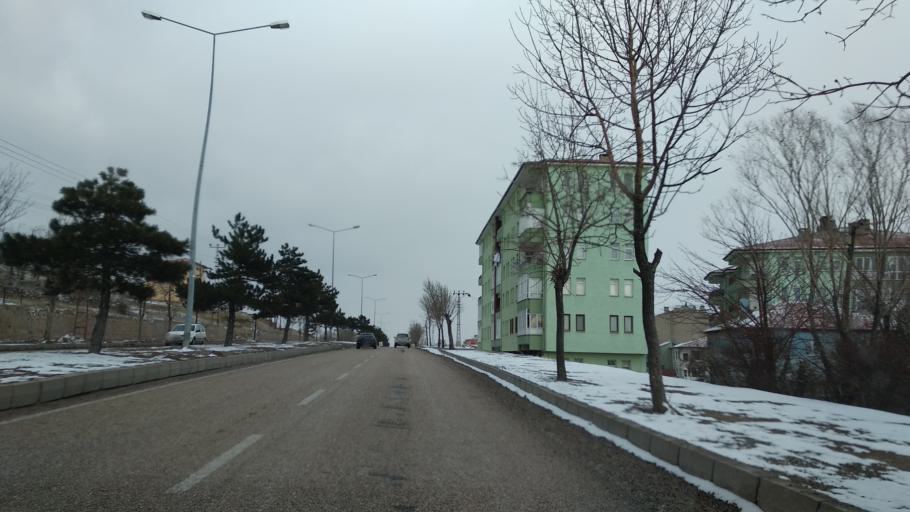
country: TR
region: Kayseri
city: Pinarbasi
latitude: 38.7242
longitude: 36.3924
